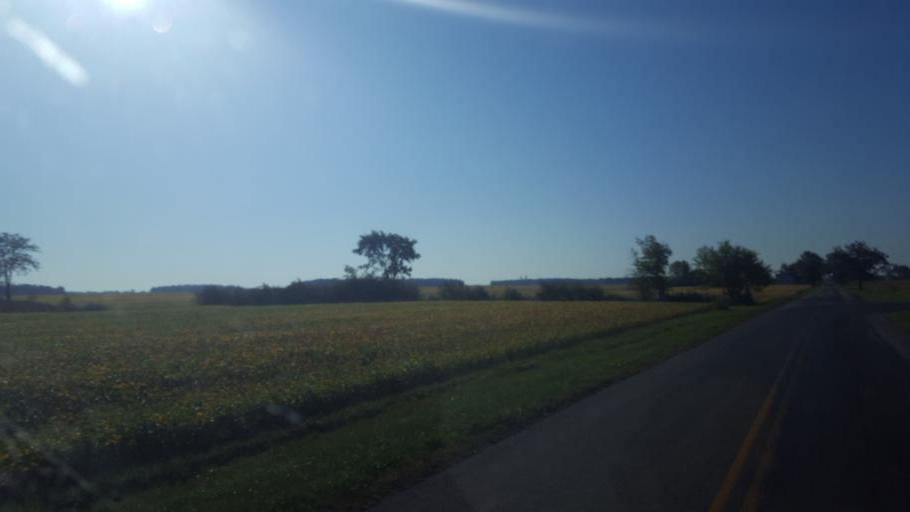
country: US
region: Ohio
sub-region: Union County
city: Richwood
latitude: 40.5165
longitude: -83.4388
